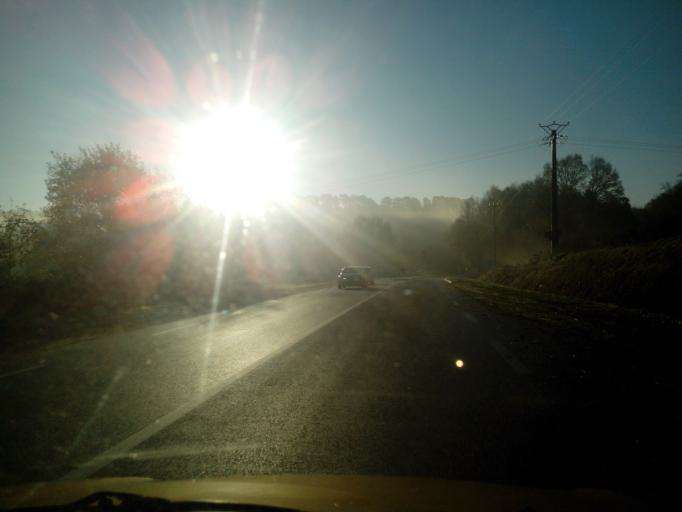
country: FR
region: Brittany
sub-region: Departement du Morbihan
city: Pluherlin
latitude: 47.7076
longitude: -2.3371
